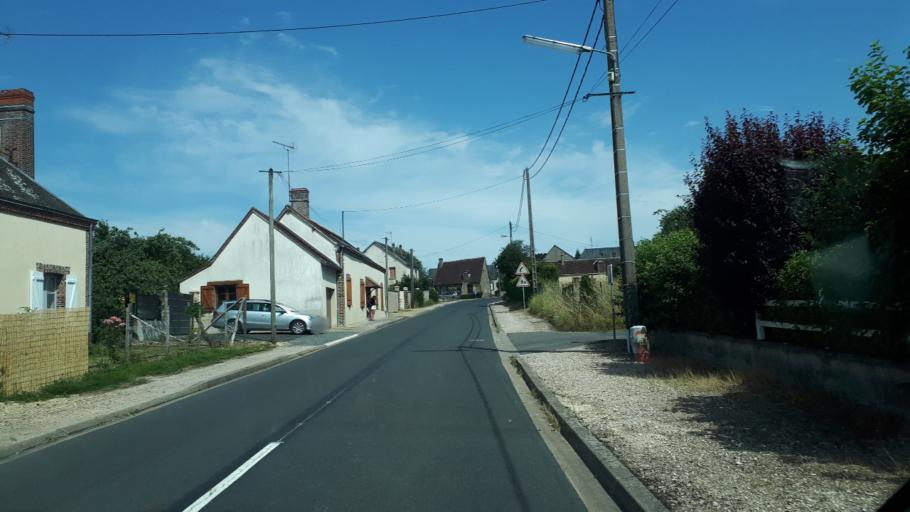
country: FR
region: Centre
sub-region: Departement du Loir-et-Cher
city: Droue
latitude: 47.9892
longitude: 1.0347
